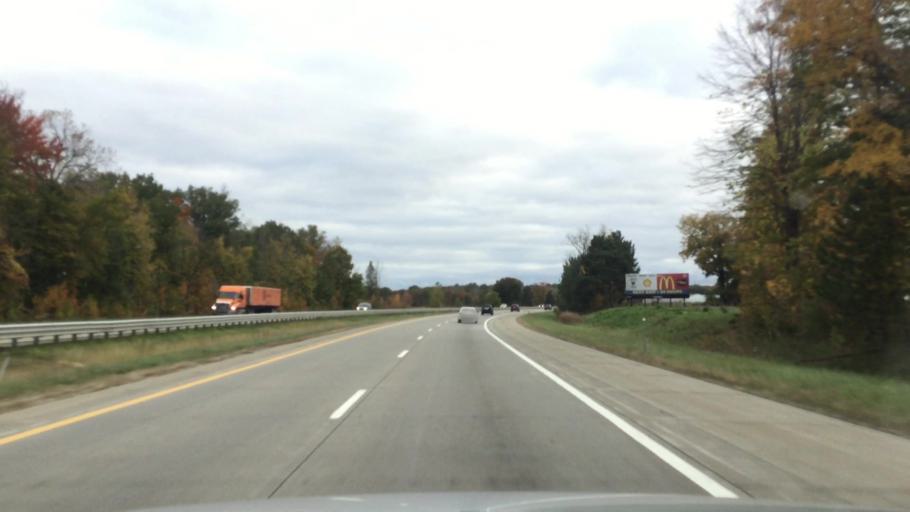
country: US
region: Michigan
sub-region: Genesee County
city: Lake Fenton
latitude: 42.8914
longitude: -83.7391
